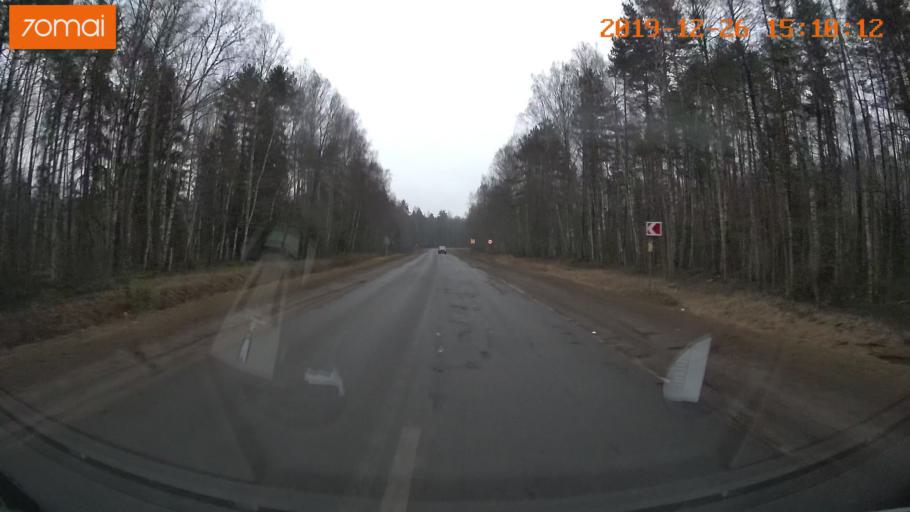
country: RU
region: Jaroslavl
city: Rybinsk
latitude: 58.1421
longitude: 38.8488
